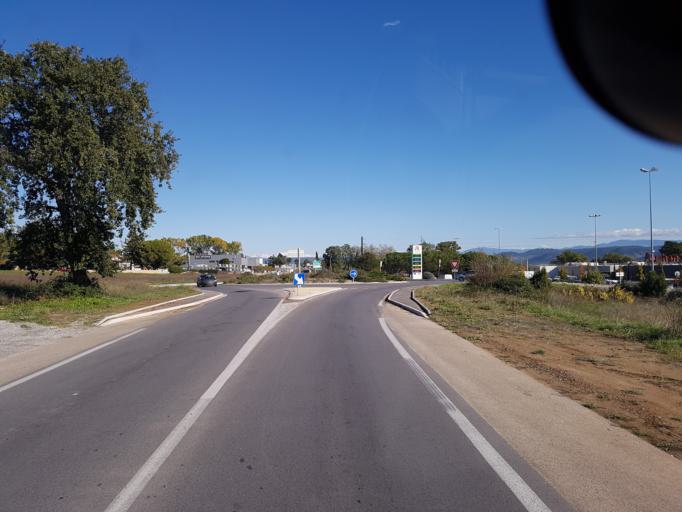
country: FR
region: Provence-Alpes-Cote d'Azur
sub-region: Departement des Alpes-de-Haute-Provence
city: Volx
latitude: 43.8500
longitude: 5.8218
